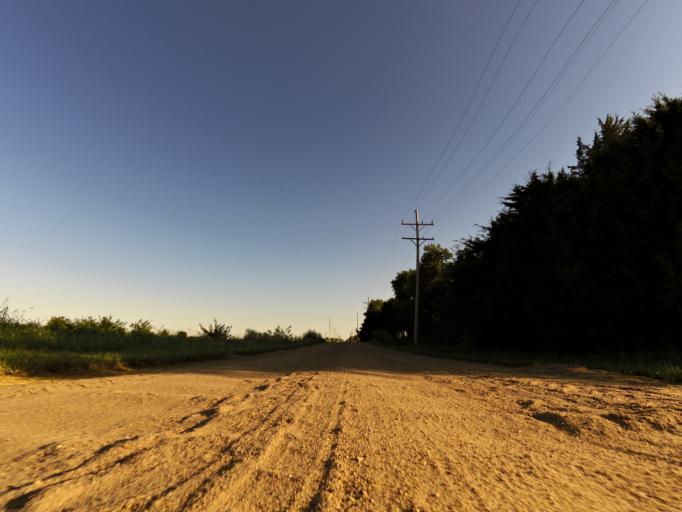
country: US
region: Kansas
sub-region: Reno County
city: South Hutchinson
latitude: 38.0058
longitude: -98.0319
